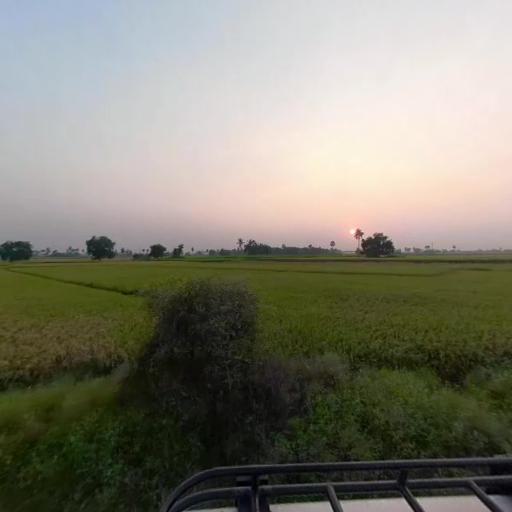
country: IN
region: Telangana
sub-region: Nalgonda
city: Suriapet
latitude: 17.0743
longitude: 79.5484
